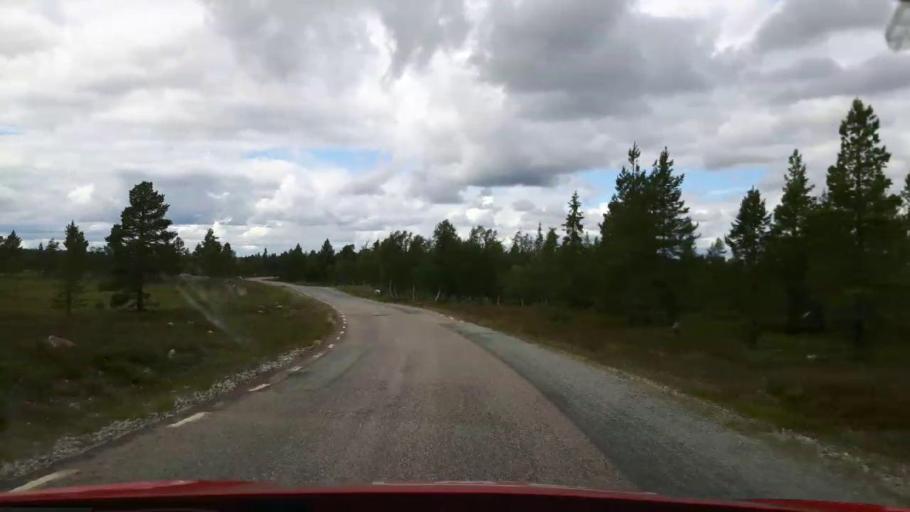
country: NO
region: Hedmark
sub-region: Engerdal
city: Engerdal
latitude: 62.2764
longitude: 12.8856
